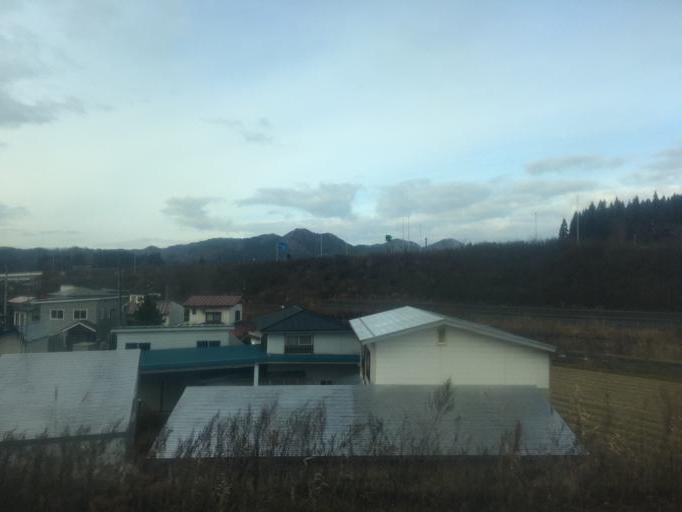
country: JP
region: Akita
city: Odate
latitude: 40.3041
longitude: 140.5694
